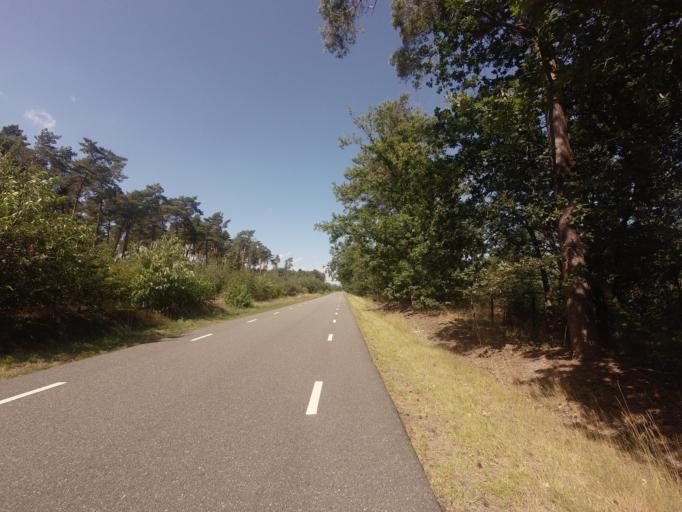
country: NL
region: Overijssel
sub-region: Gemeente Twenterand
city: Den Ham
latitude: 52.5433
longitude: 6.4430
